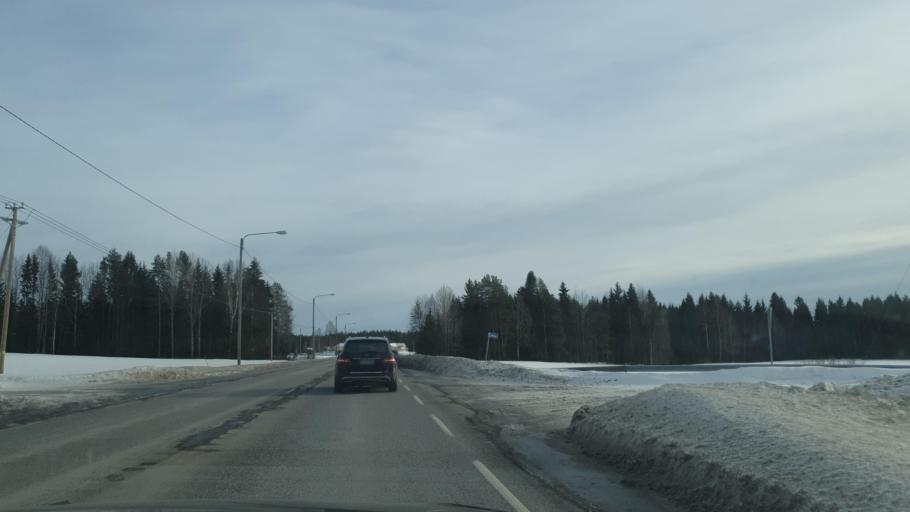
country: FI
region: Northern Ostrobothnia
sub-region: Oulu
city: Muhos
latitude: 64.7893
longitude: 26.1343
